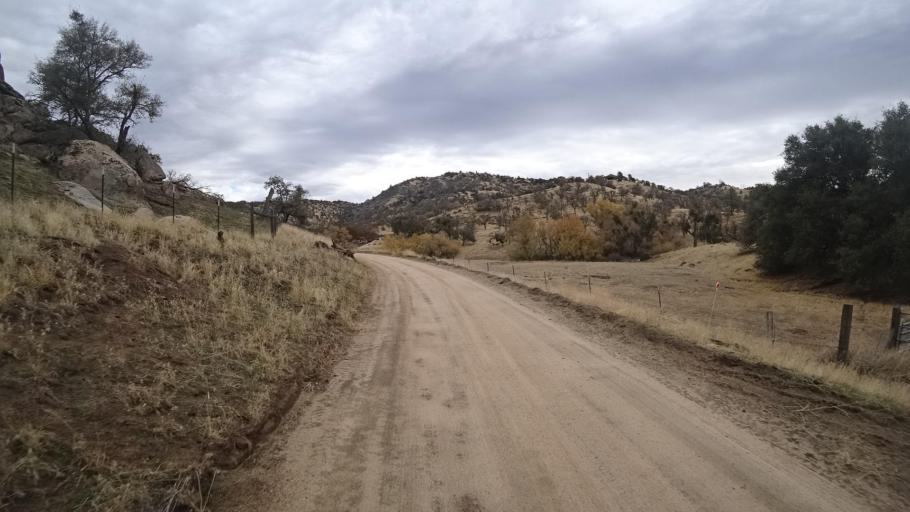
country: US
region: California
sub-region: Kern County
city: Stallion Springs
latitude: 35.1103
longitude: -118.6773
